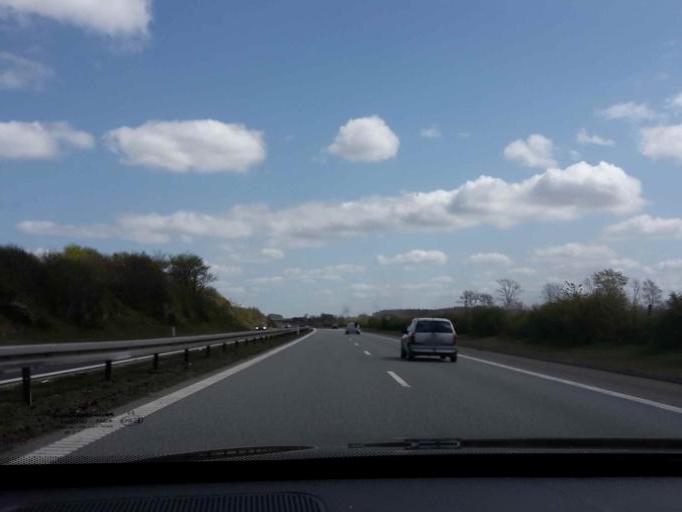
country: DK
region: South Denmark
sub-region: Vejen Kommune
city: Holsted
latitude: 55.5118
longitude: 8.9614
